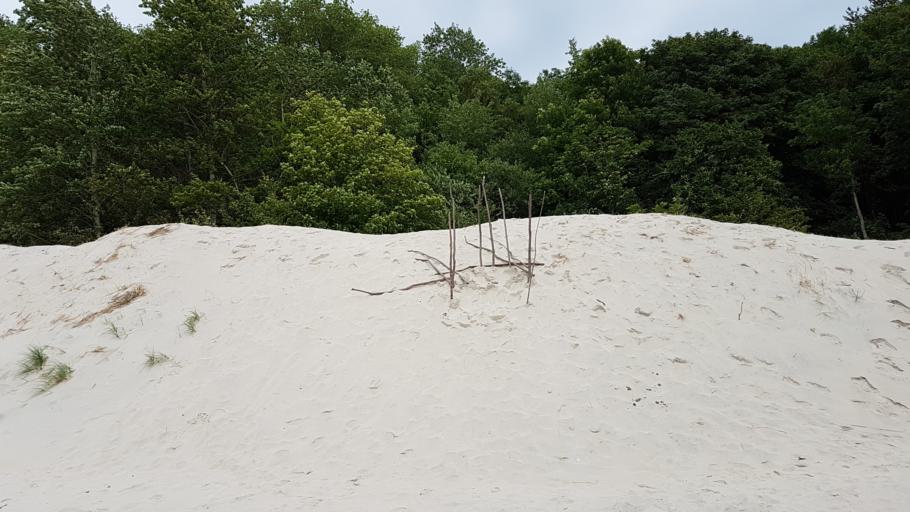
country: RU
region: Kaliningrad
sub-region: Gorod Kaliningrad
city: Yantarnyy
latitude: 54.8706
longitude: 19.9338
